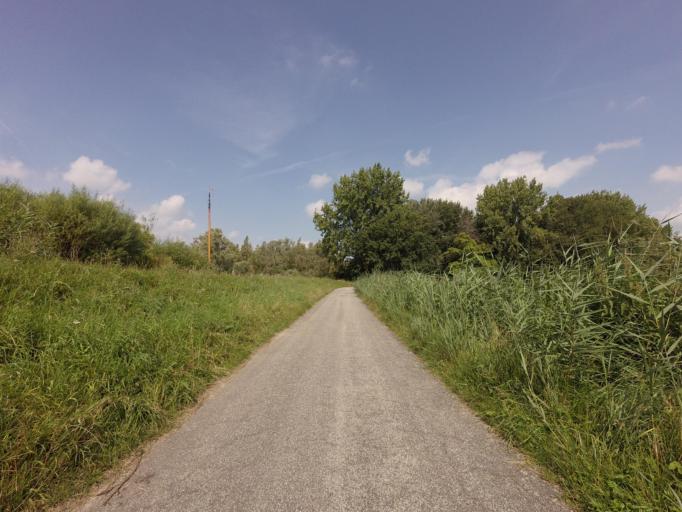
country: NL
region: South Holland
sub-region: Gemeente Sliedrecht
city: Sliedrecht
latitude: 51.8050
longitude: 4.7658
